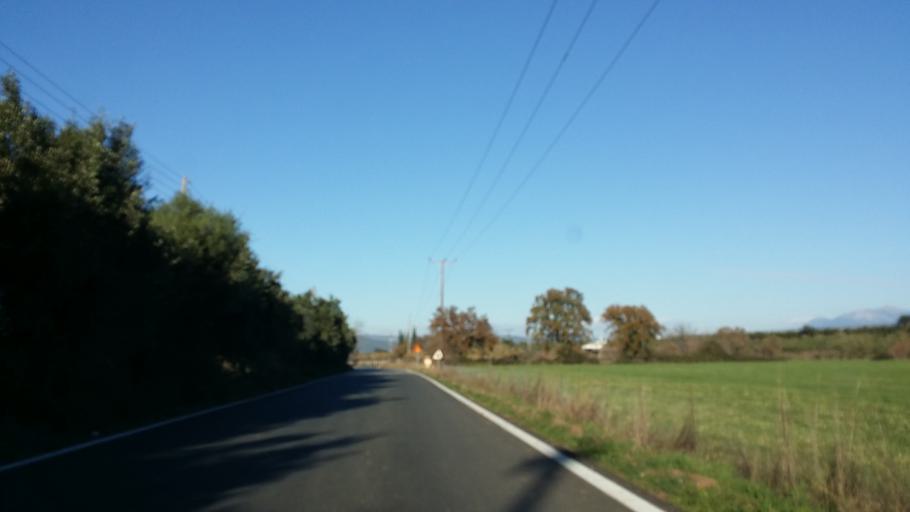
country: GR
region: West Greece
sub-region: Nomos Aitolias kai Akarnanias
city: Angelokastro
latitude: 38.6216
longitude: 21.2292
